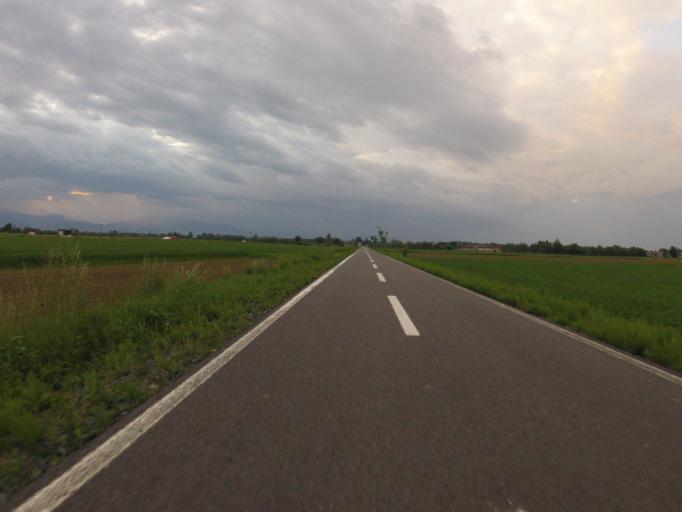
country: IT
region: Piedmont
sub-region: Provincia di Torino
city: Villafranca Piemonte
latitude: 44.7996
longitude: 7.5048
